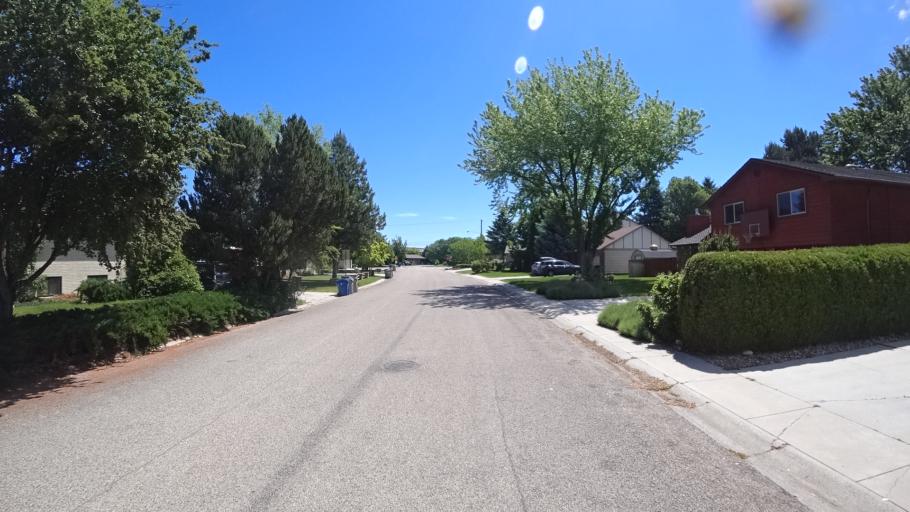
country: US
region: Idaho
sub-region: Ada County
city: Boise
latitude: 43.5766
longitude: -116.2248
